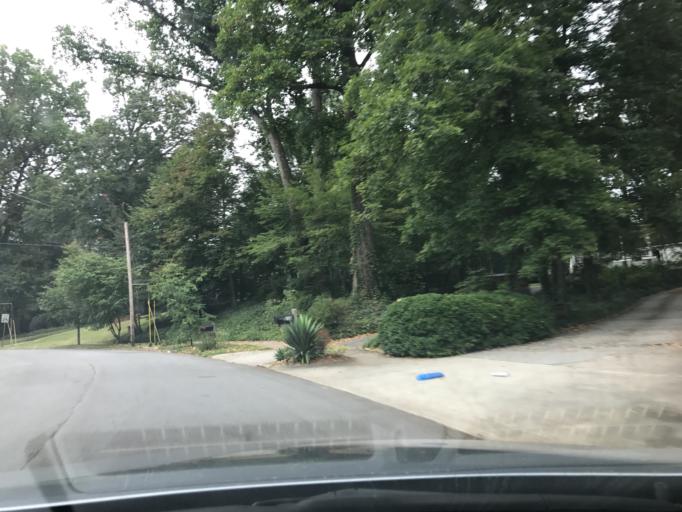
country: US
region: Georgia
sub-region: DeKalb County
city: Decatur
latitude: 33.7674
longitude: -84.3119
